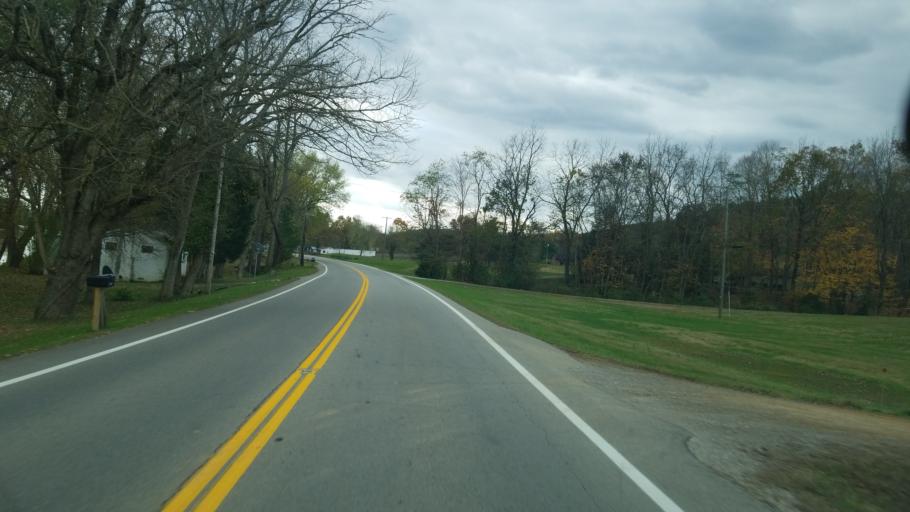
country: US
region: Ohio
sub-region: Scioto County
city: Lucasville
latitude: 38.9494
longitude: -83.0459
